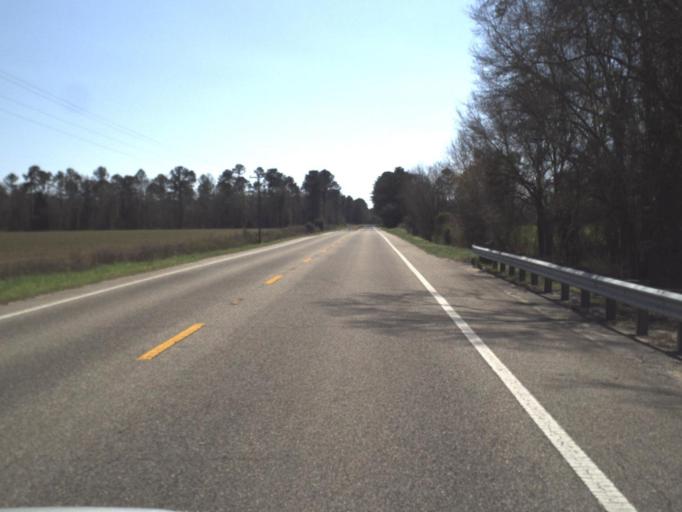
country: US
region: Florida
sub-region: Calhoun County
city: Blountstown
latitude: 30.5653
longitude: -85.0217
